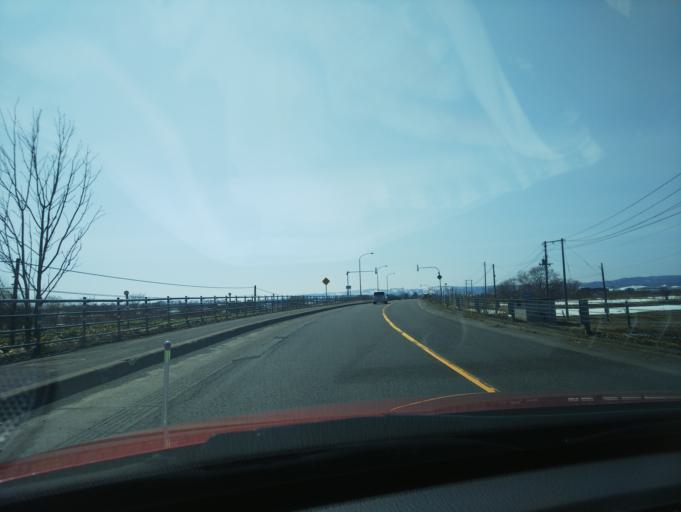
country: JP
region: Hokkaido
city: Nayoro
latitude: 44.3142
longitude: 142.4565
